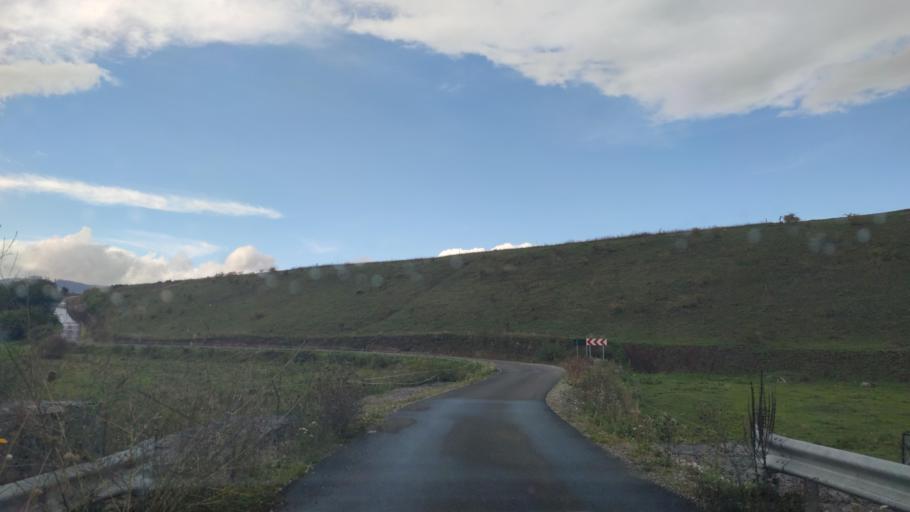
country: RO
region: Harghita
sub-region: Comuna Remetea
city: Remetea
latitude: 46.8141
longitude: 25.3866
